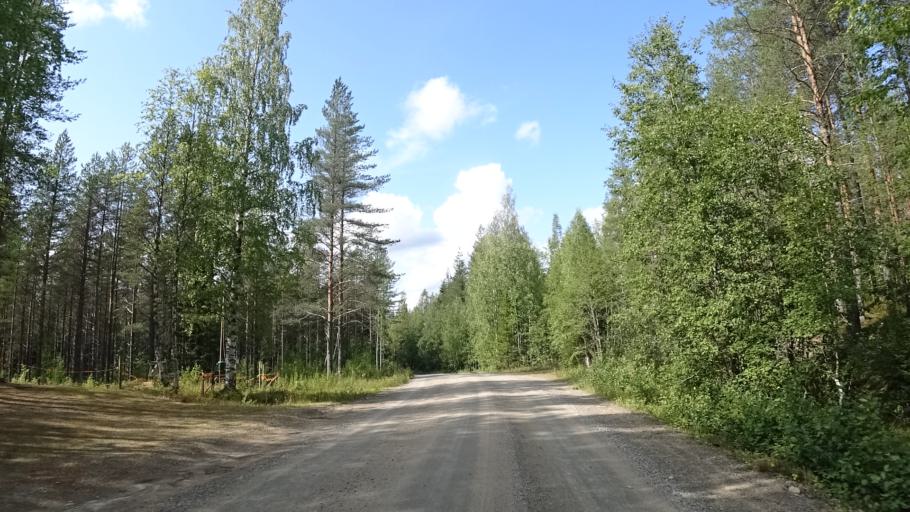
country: FI
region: North Karelia
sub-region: Joensuu
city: Ilomantsi
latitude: 62.9210
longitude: 31.3415
